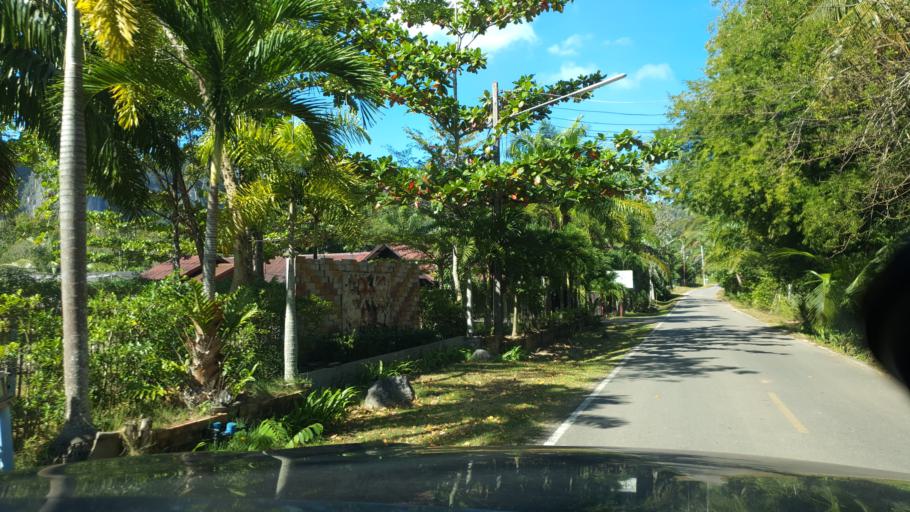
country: TH
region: Phangnga
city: Ban Ao Nang
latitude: 8.0300
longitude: 98.8587
